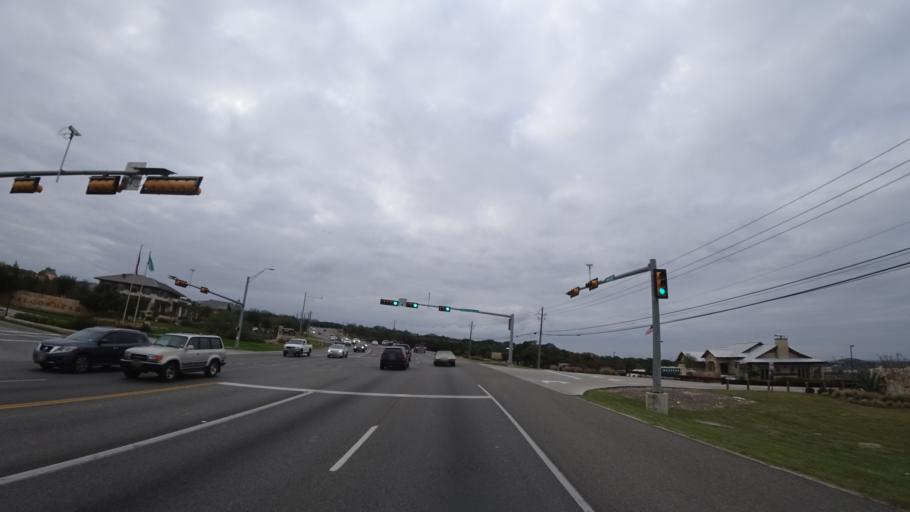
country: US
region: Texas
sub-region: Travis County
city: Bee Cave
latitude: 30.3249
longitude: -97.9579
